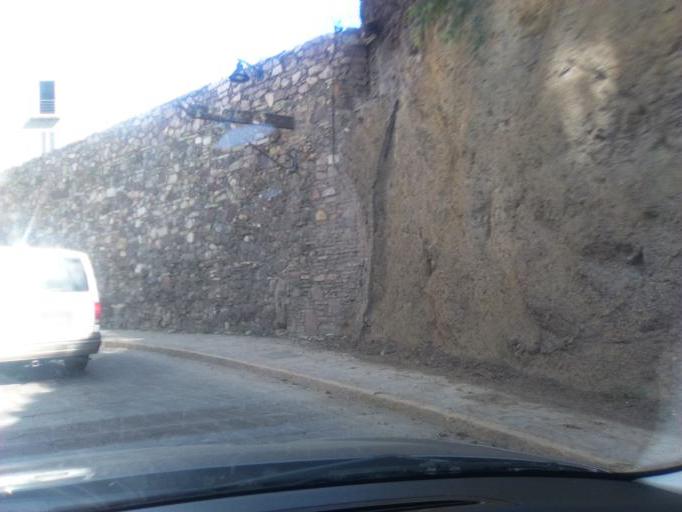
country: MX
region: Guanajuato
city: Guanajuato
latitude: 21.0186
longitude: -101.2620
